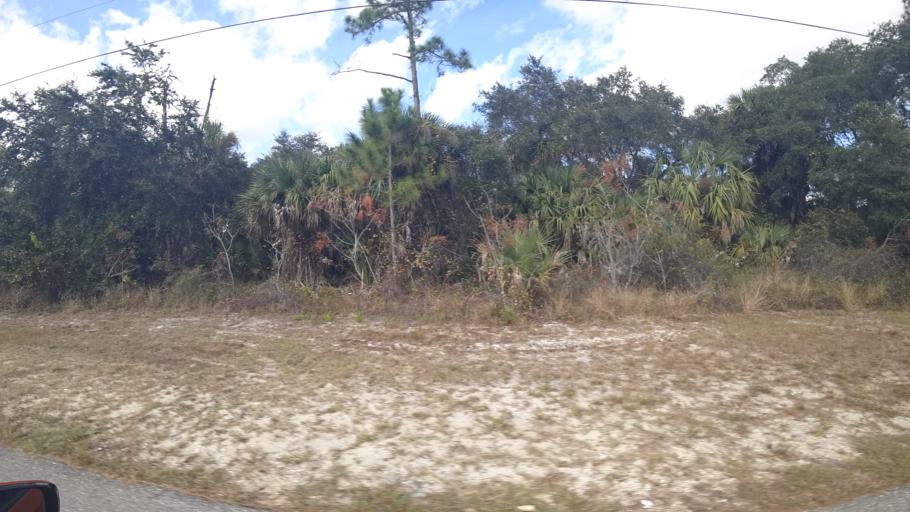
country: US
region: Florida
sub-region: Charlotte County
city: Port Charlotte
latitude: 27.0440
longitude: -82.1340
